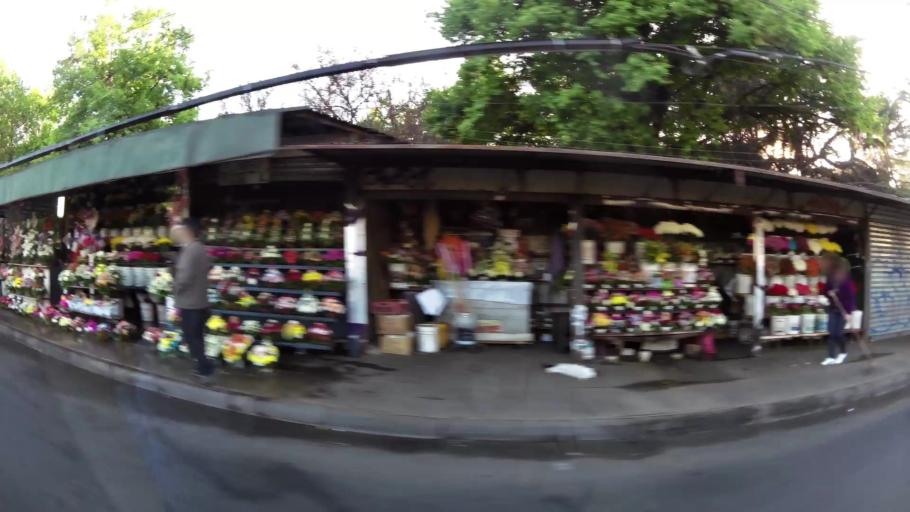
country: CL
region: Santiago Metropolitan
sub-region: Provincia de Santiago
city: Santiago
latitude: -33.3861
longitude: -70.6362
